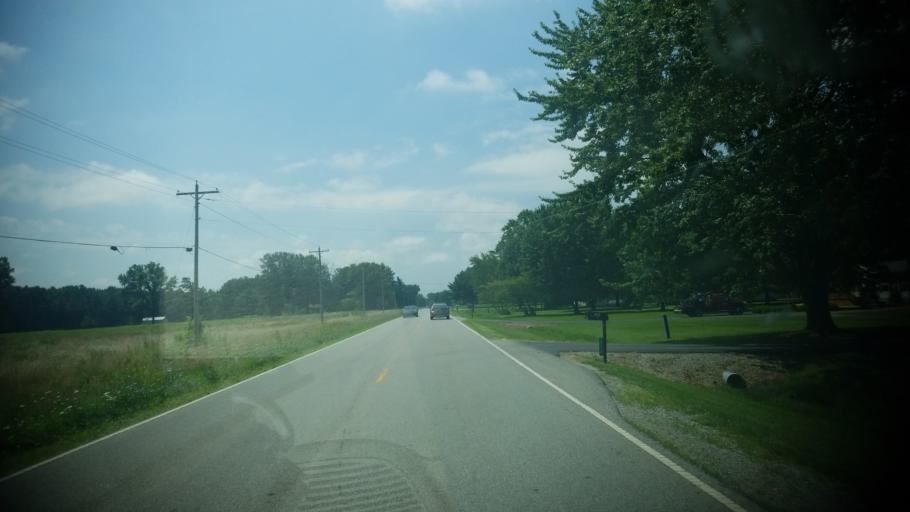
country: US
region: Illinois
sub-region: Wayne County
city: Fairfield
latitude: 38.3960
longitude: -88.3506
